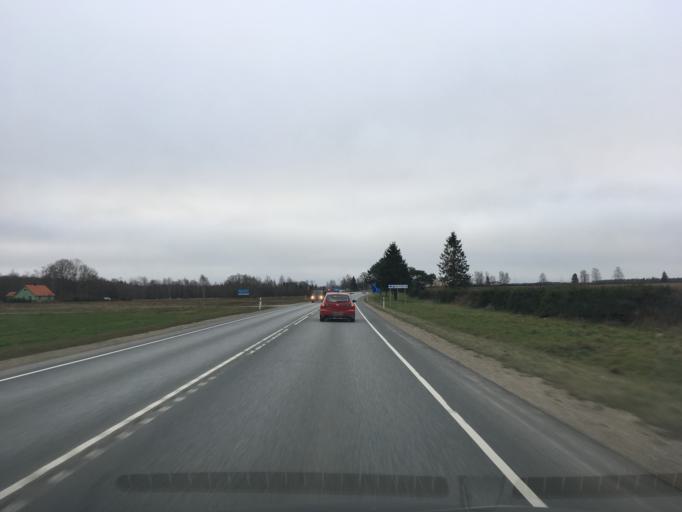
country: EE
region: Laeaene-Virumaa
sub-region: Someru vald
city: Someru
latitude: 59.3704
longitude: 26.4288
